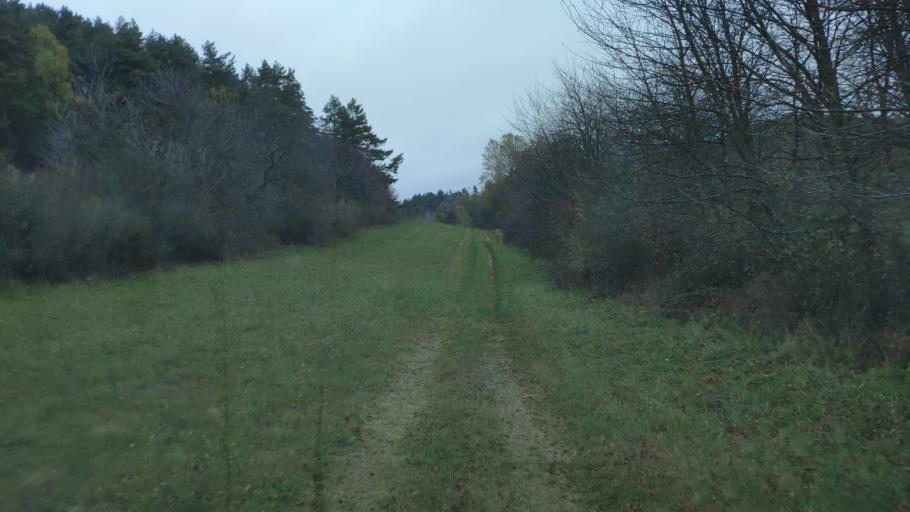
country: SK
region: Presovsky
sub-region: Okres Presov
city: Presov
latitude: 48.9313
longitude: 21.0985
